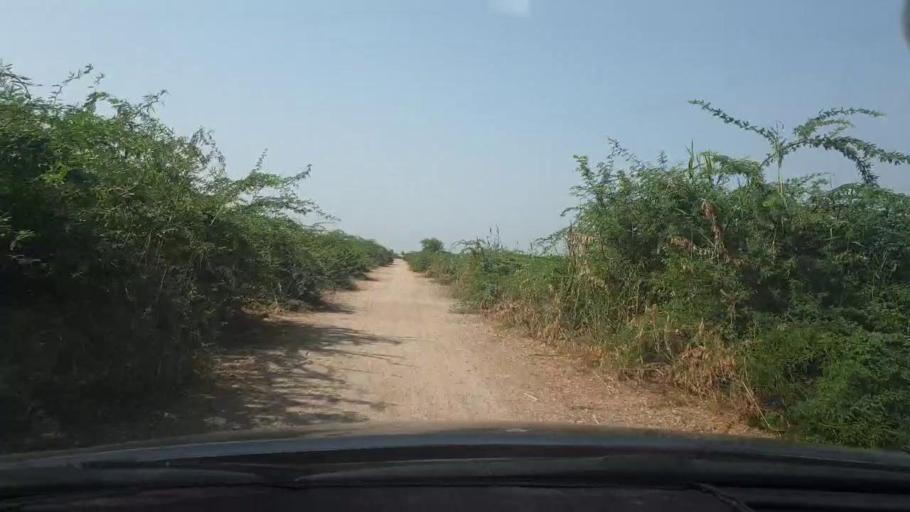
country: PK
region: Sindh
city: Tando Bago
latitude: 24.7190
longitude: 69.0943
